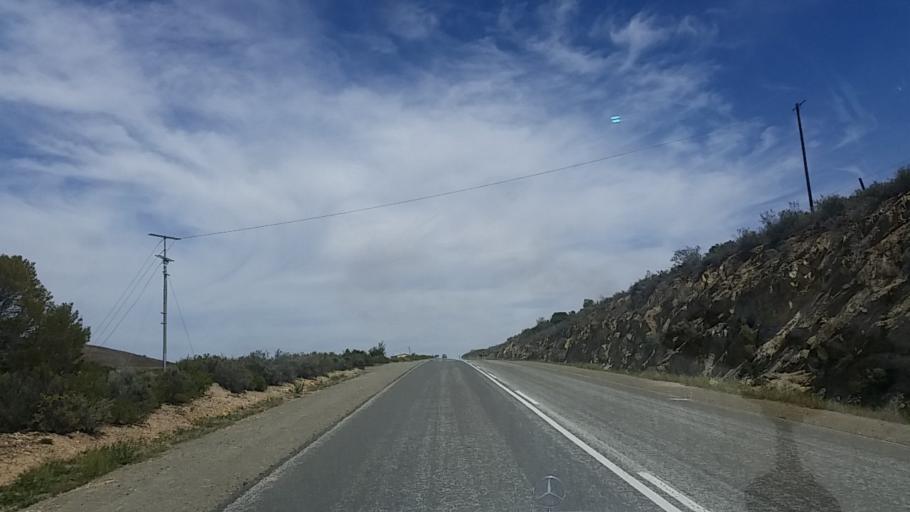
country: ZA
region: Western Cape
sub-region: Eden District Municipality
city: Knysna
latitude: -33.6563
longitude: 23.1182
